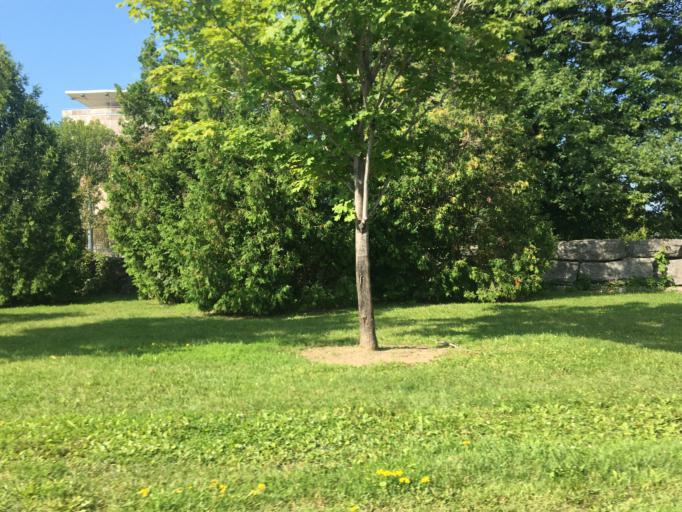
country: CA
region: Ontario
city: Ottawa
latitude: 45.3794
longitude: -75.6858
